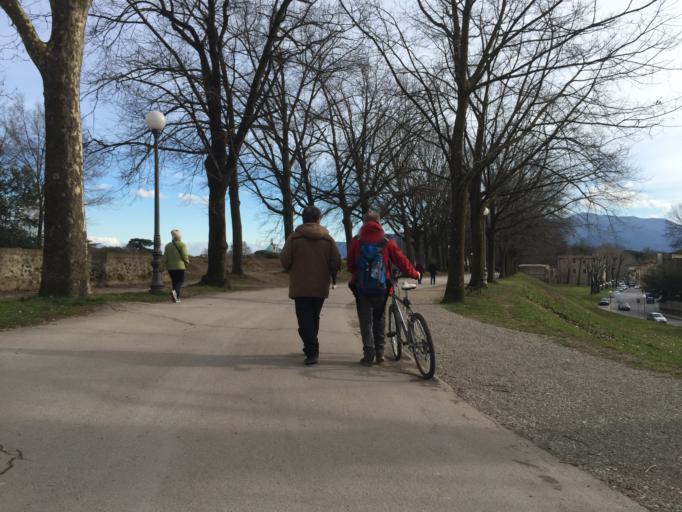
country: IT
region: Tuscany
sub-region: Provincia di Lucca
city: Lucca
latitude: 43.8483
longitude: 10.5138
